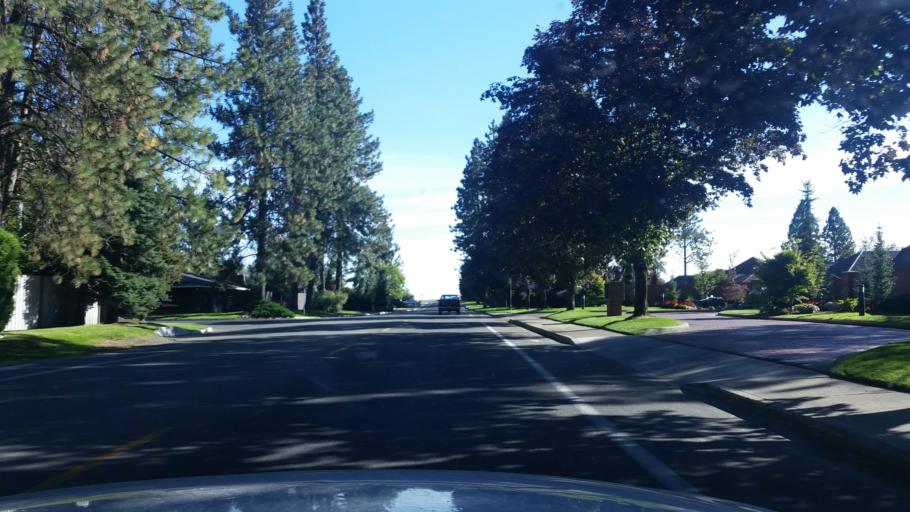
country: US
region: Washington
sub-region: Spokane County
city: Spokane
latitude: 47.6059
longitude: -117.3953
